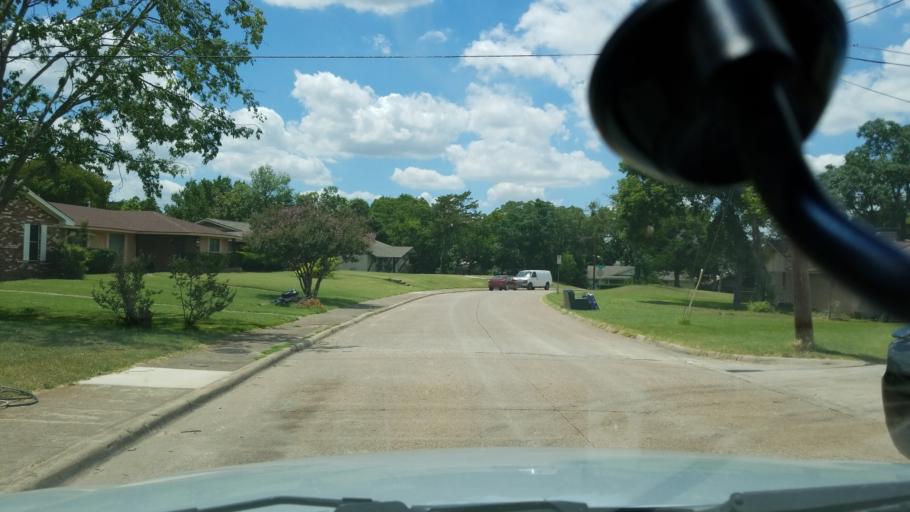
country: US
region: Texas
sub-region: Dallas County
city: Cockrell Hill
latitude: 32.6992
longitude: -96.8812
